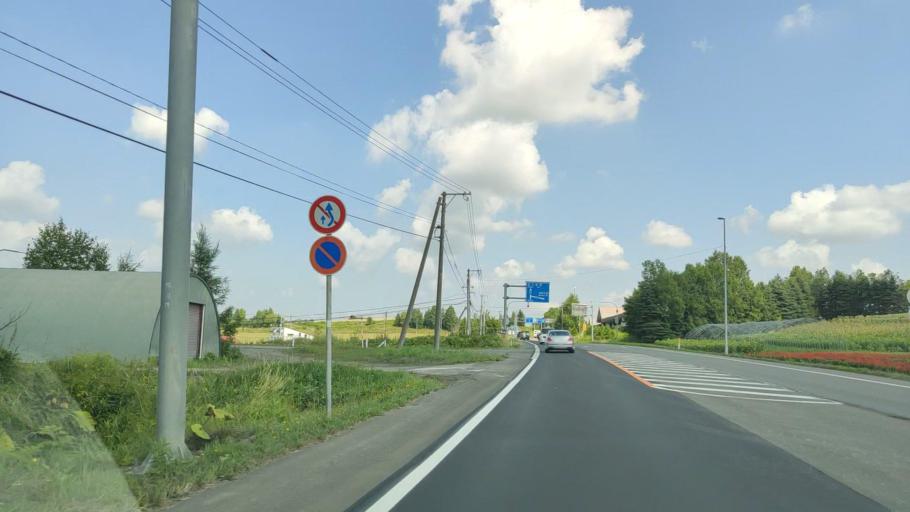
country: JP
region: Hokkaido
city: Shimo-furano
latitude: 43.5429
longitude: 142.4387
